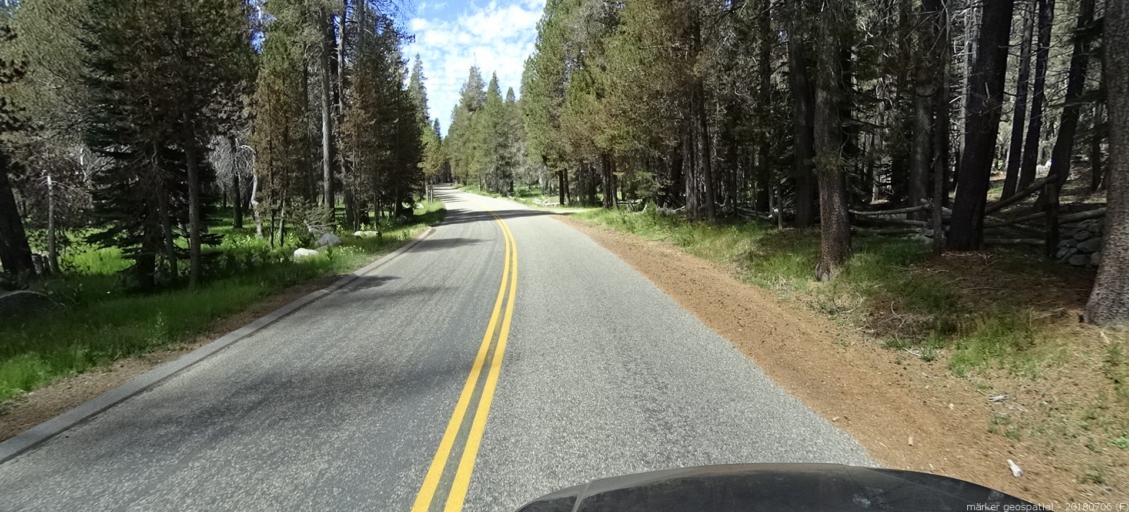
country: US
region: California
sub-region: Madera County
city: Oakhurst
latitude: 37.4477
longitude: -119.4669
